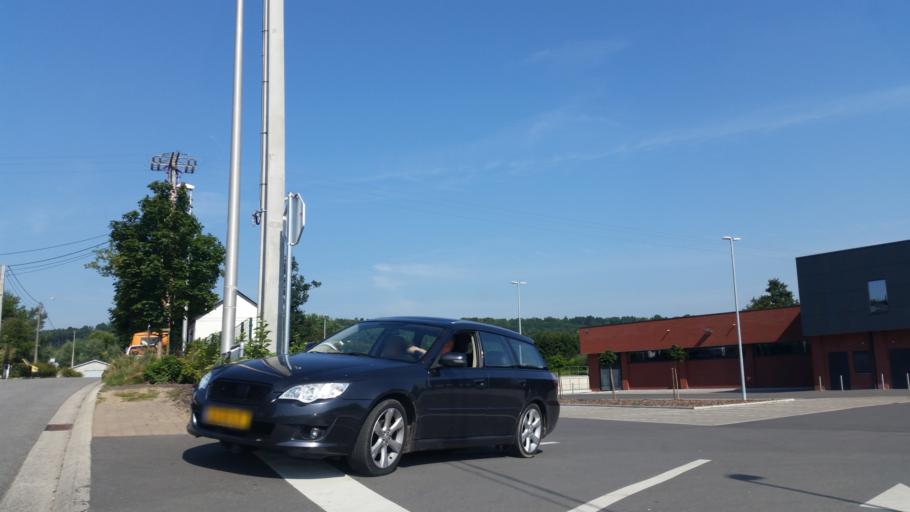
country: BE
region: Wallonia
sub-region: Province du Luxembourg
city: Durbuy
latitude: 50.3414
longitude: 5.4851
